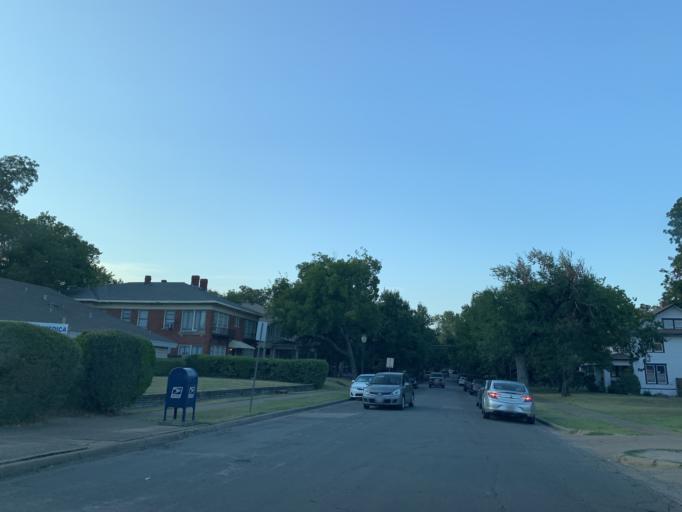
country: US
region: Texas
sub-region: Dallas County
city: Cockrell Hill
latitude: 32.7444
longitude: -96.8441
